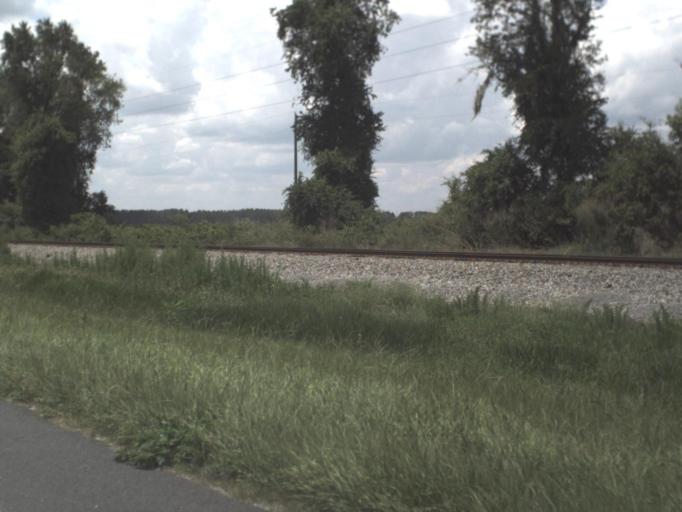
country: US
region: Florida
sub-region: Suwannee County
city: Wellborn
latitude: 30.3921
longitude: -82.8269
